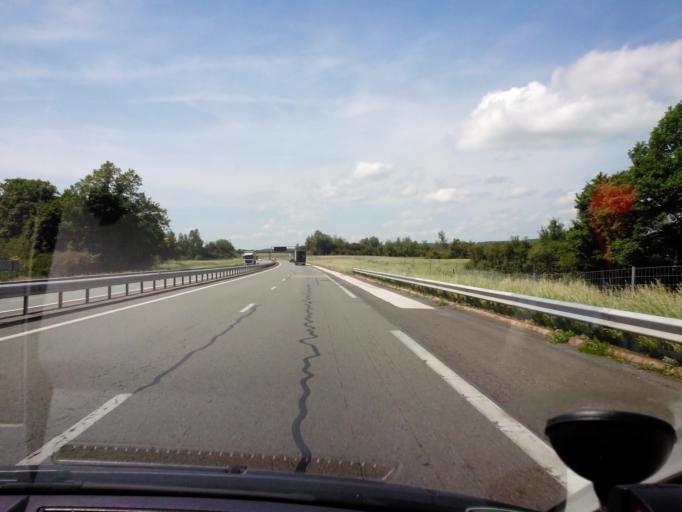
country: FR
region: Champagne-Ardenne
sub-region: Departement de la Haute-Marne
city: Avrecourt
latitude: 48.0198
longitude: 5.5295
